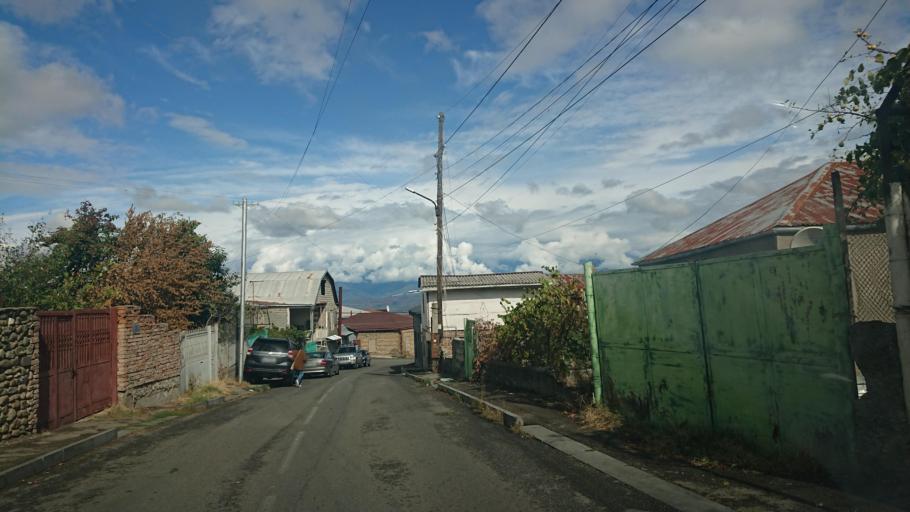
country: GE
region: Kakheti
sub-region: Telavi
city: Telavi
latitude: 41.9125
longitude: 45.4708
